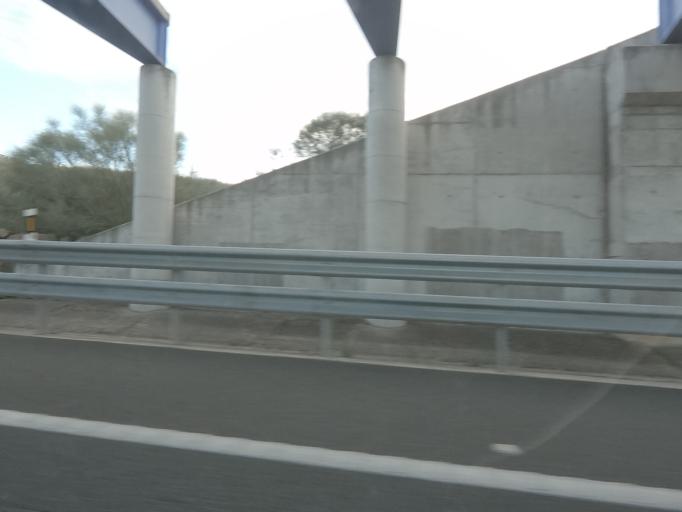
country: ES
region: Extremadura
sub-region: Provincia de Caceres
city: Caceres
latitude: 39.4533
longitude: -6.4173
